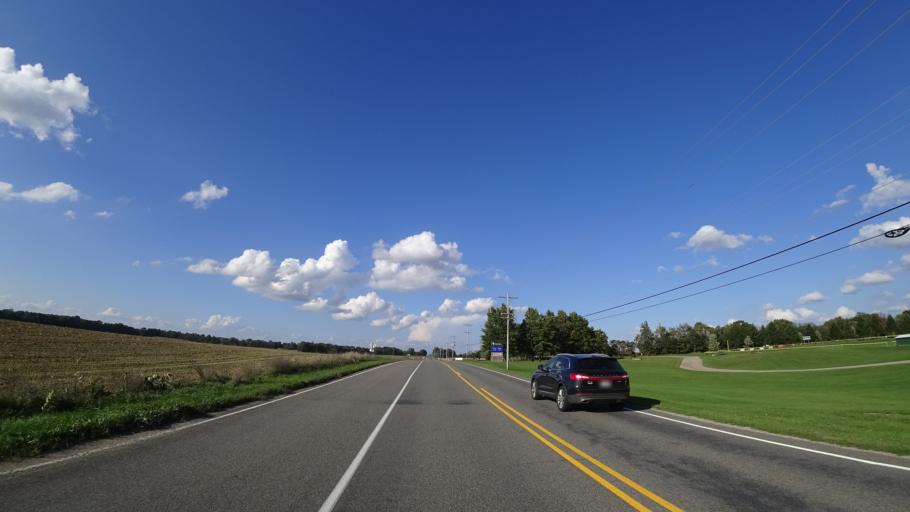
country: US
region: Michigan
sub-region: Saint Joseph County
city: Centreville
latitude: 41.8917
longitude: -85.5069
